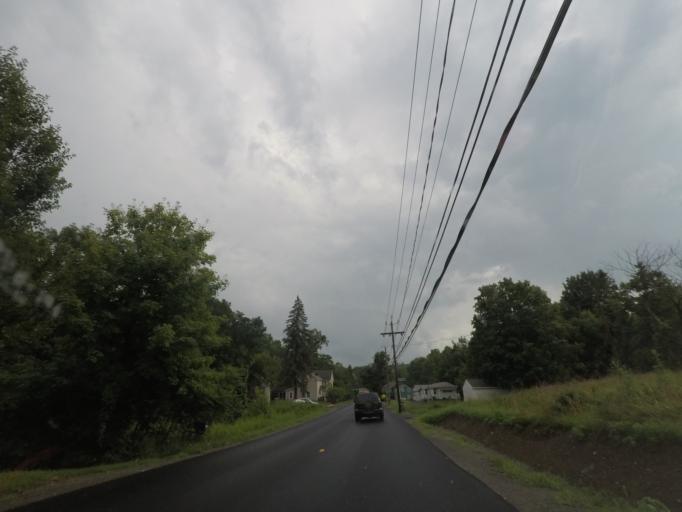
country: US
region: New York
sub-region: Rensselaer County
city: Poestenkill
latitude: 42.6851
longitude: -73.5408
